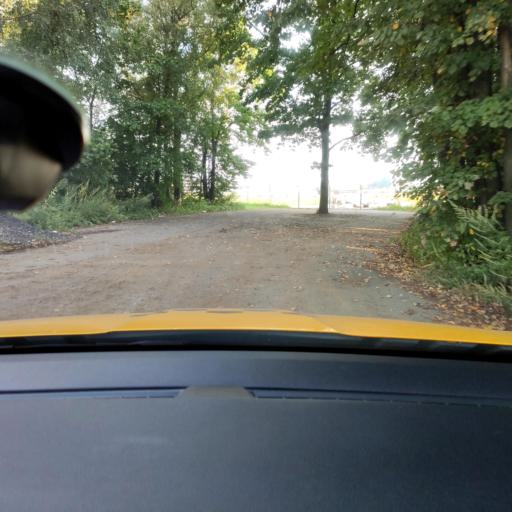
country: RU
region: Moskovskaya
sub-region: Leninskiy Rayon
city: Vnukovo
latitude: 55.5946
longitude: 37.2946
